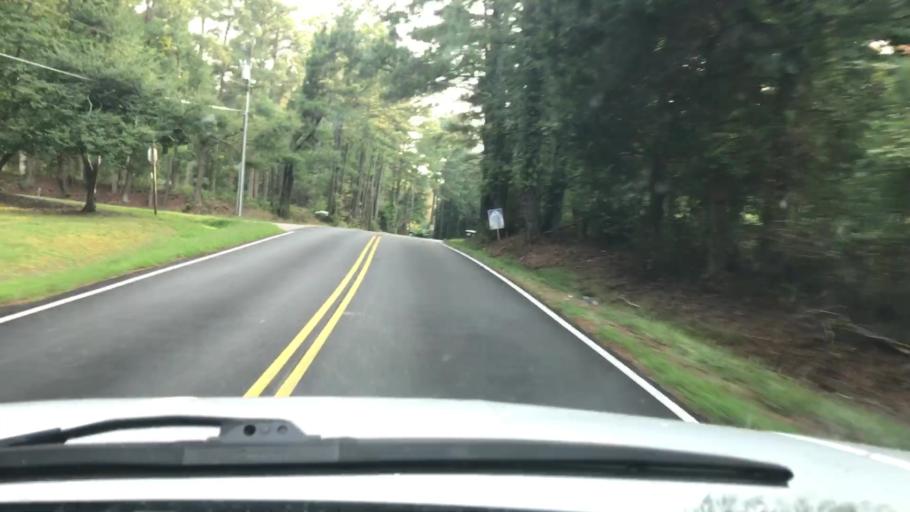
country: US
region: Virginia
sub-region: Chesterfield County
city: Chesterfield
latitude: 37.4169
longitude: -77.5439
